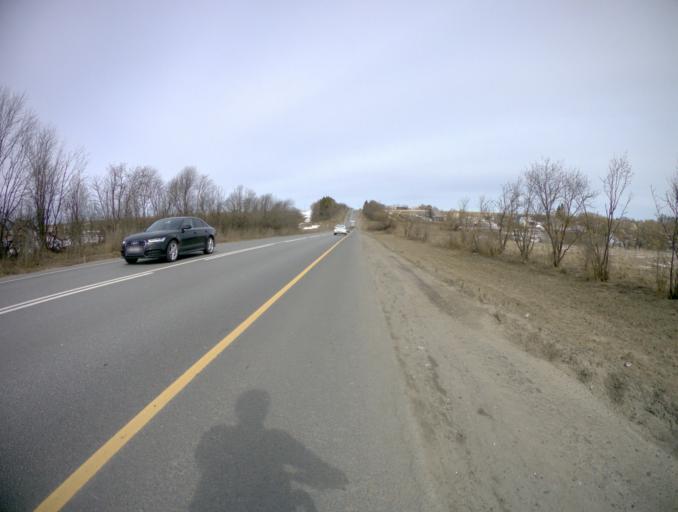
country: RU
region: Vladimir
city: Bogolyubovo
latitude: 56.2739
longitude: 40.4657
